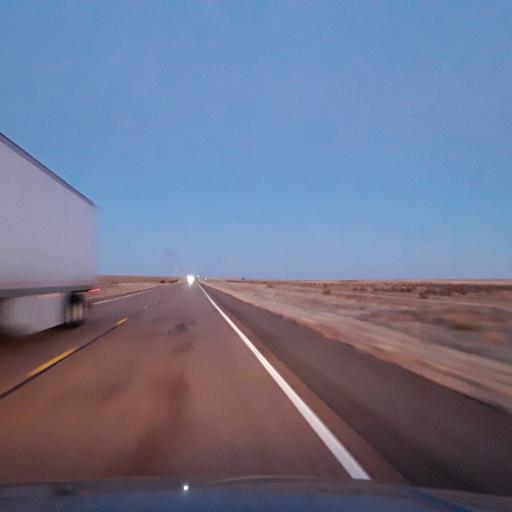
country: US
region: New Mexico
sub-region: Guadalupe County
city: Santa Rosa
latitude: 34.7637
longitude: -104.9820
